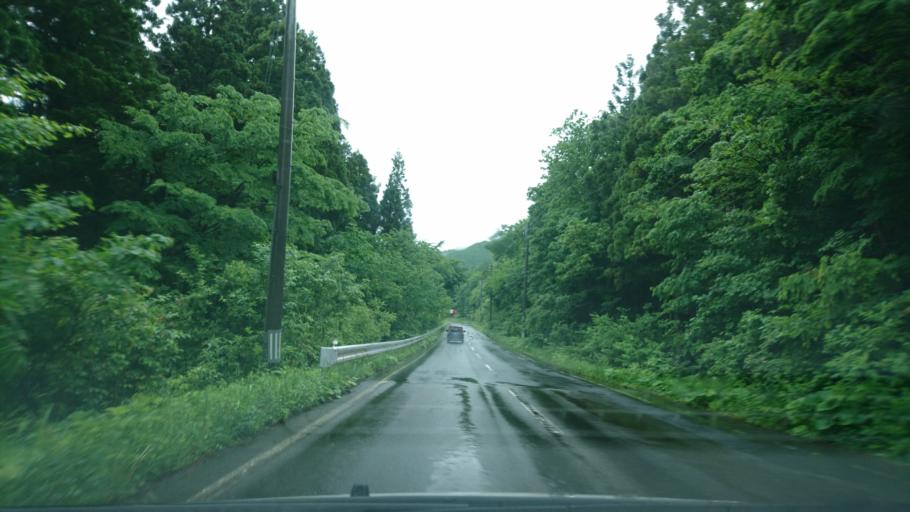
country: JP
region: Iwate
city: Ichinoseki
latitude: 39.0097
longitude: 140.8912
